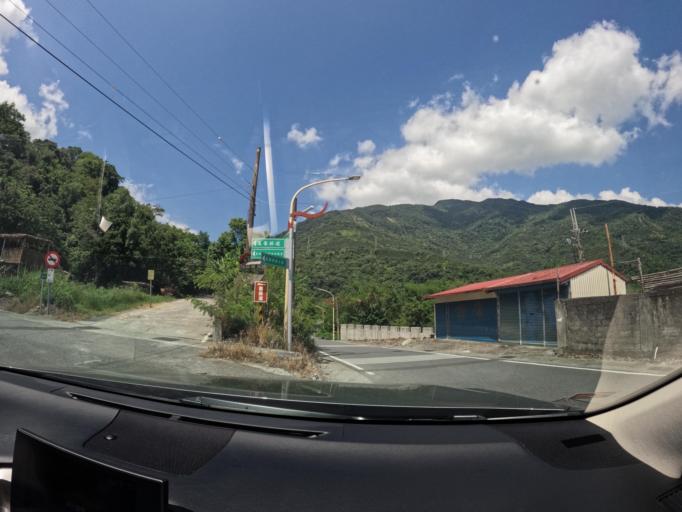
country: TW
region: Taiwan
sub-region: Hualien
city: Hualian
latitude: 23.7171
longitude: 121.4084
